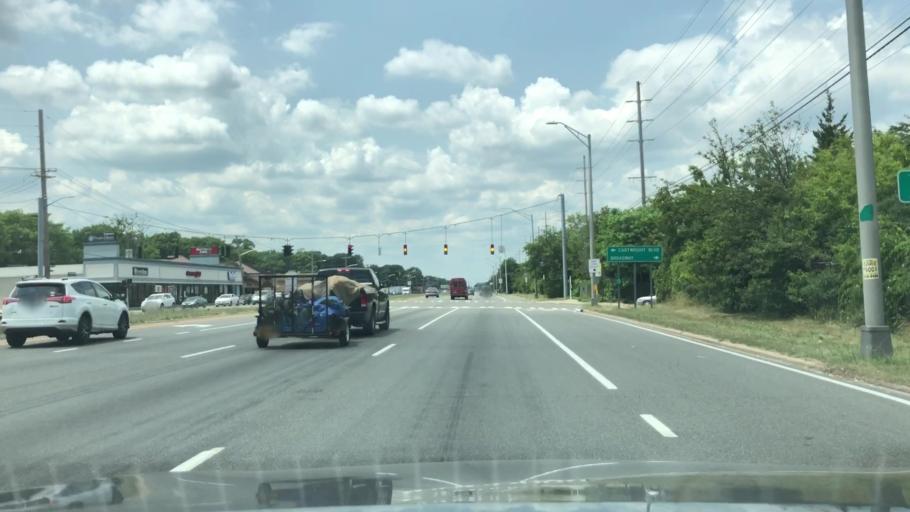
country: US
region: New York
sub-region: Nassau County
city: Massapequa Park
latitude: 40.6781
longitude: -73.4474
